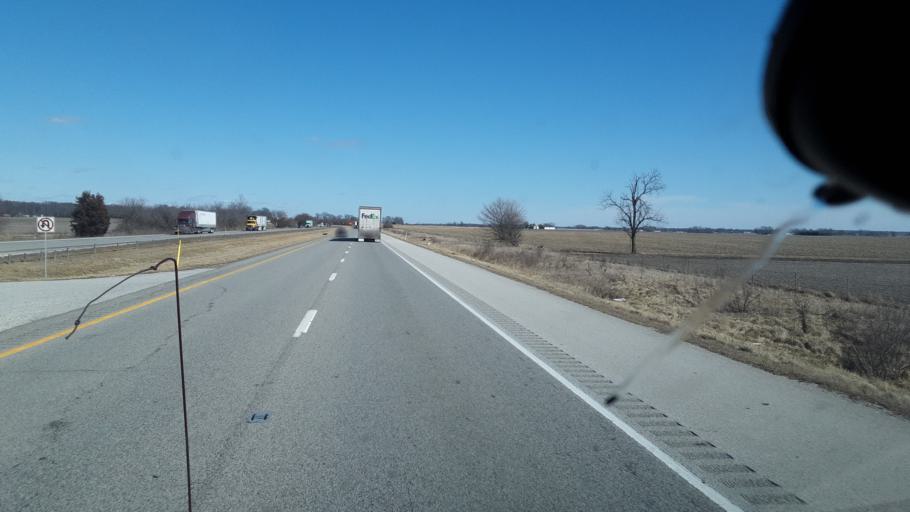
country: US
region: Indiana
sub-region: Morgan County
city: Monrovia
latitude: 39.5927
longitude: -86.5421
